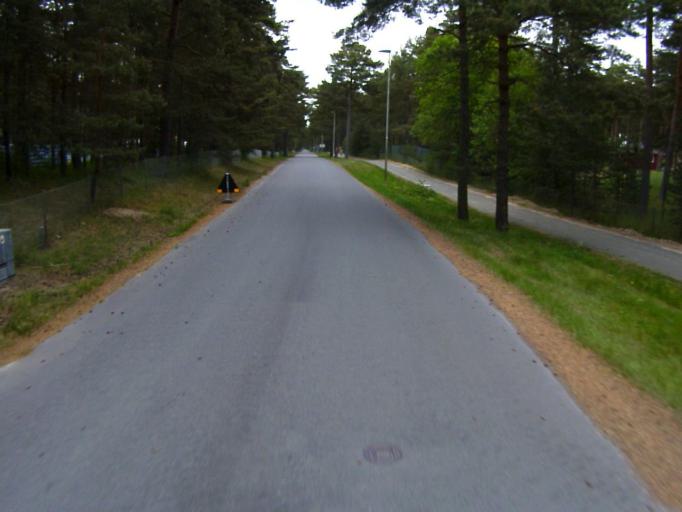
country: SE
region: Skane
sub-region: Kristianstads Kommun
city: Ahus
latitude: 55.9400
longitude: 14.3169
